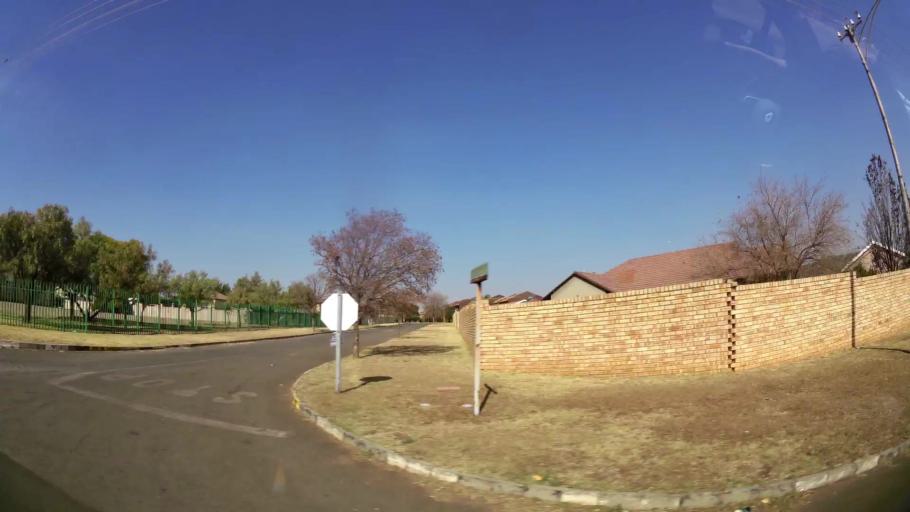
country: ZA
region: Gauteng
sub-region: West Rand District Municipality
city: Randfontein
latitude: -26.1569
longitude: 27.6975
